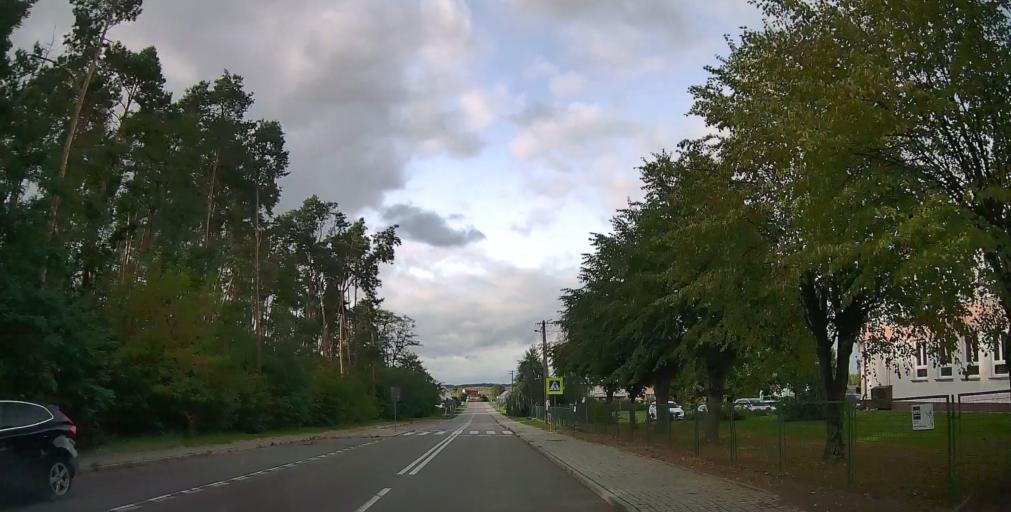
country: PL
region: Masovian Voivodeship
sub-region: Powiat grojecki
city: Jasieniec
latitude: 51.7536
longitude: 20.9613
